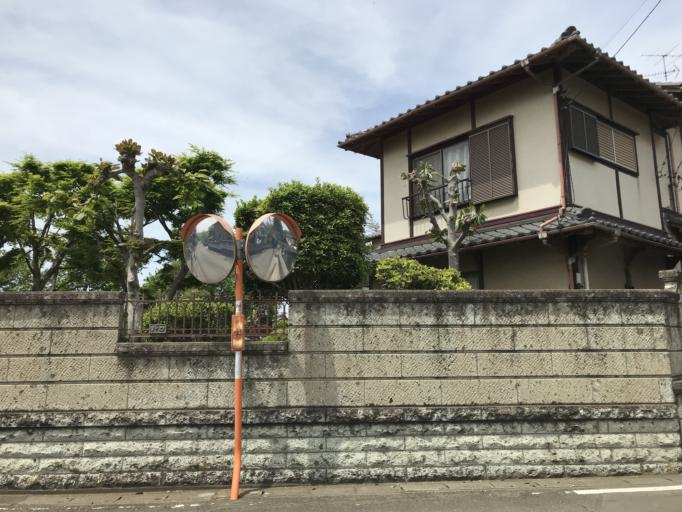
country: JP
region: Ibaraki
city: Mitsukaido
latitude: 35.9686
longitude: 139.9558
